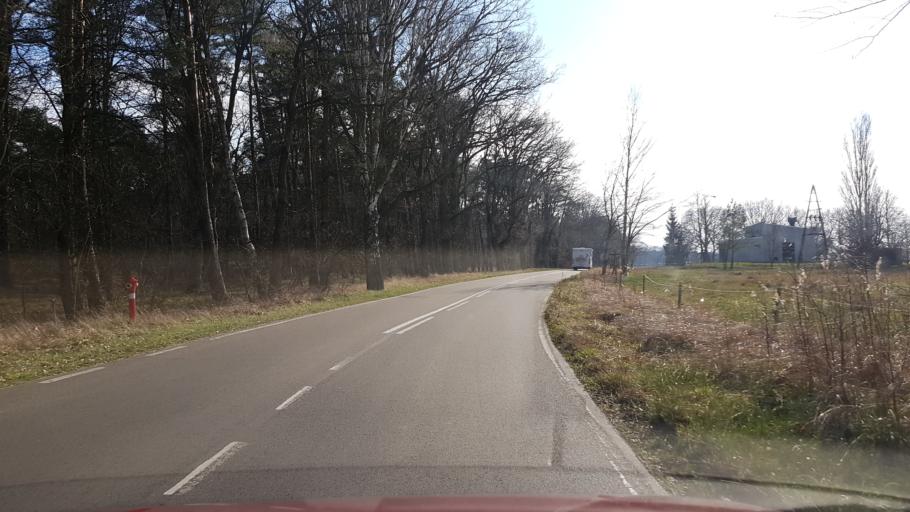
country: PL
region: West Pomeranian Voivodeship
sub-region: Powiat policki
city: Nowe Warpno
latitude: 53.7278
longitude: 14.3122
